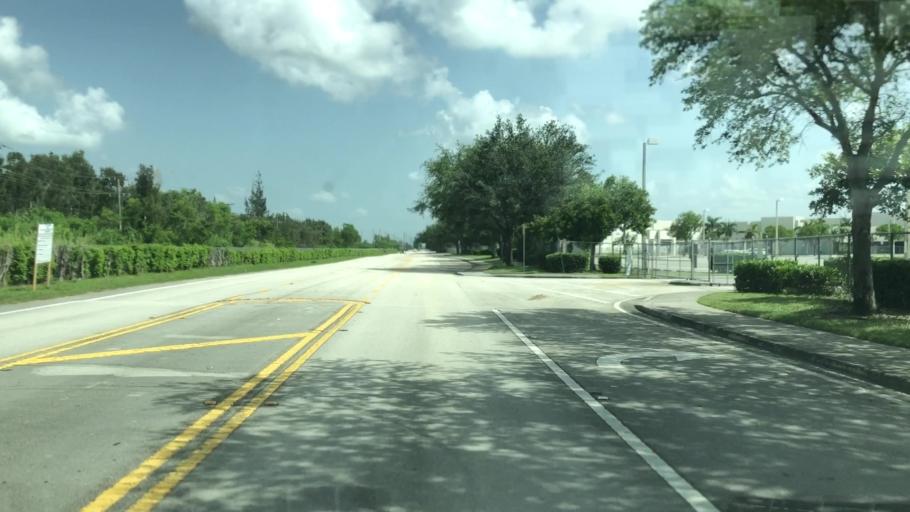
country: US
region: Florida
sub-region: Miami-Dade County
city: Palm Springs North
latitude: 25.9670
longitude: -80.3753
